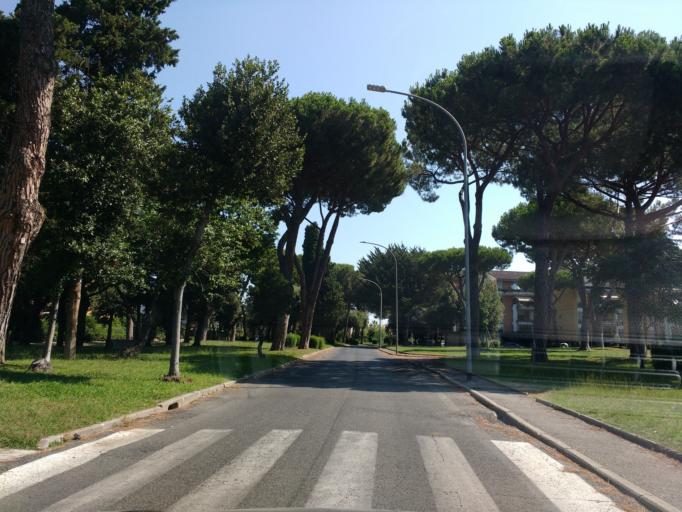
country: IT
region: Latium
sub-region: Citta metropolitana di Roma Capitale
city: Acilia-Castel Fusano-Ostia Antica
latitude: 41.7560
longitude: 12.3537
